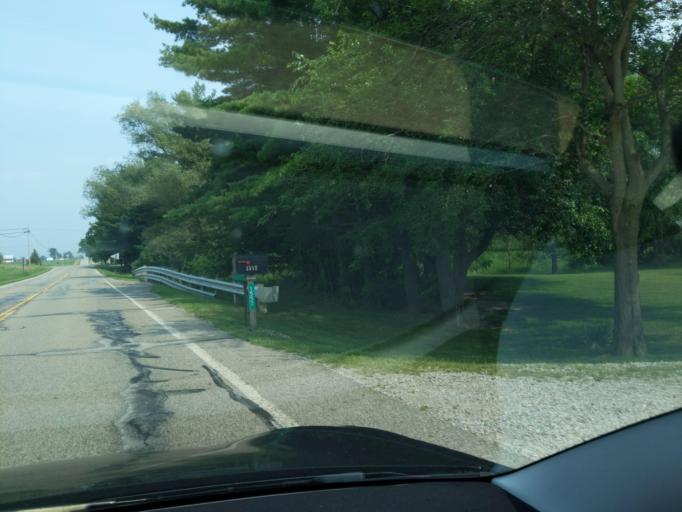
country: US
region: Michigan
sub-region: Clinton County
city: Saint Johns
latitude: 42.9290
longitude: -84.5545
